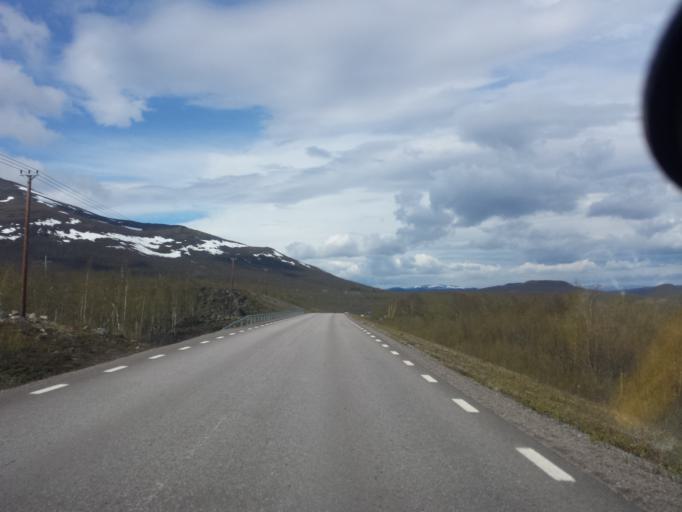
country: SE
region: Norrbotten
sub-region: Kiruna Kommun
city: Kiruna
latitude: 68.1561
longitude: 19.7768
